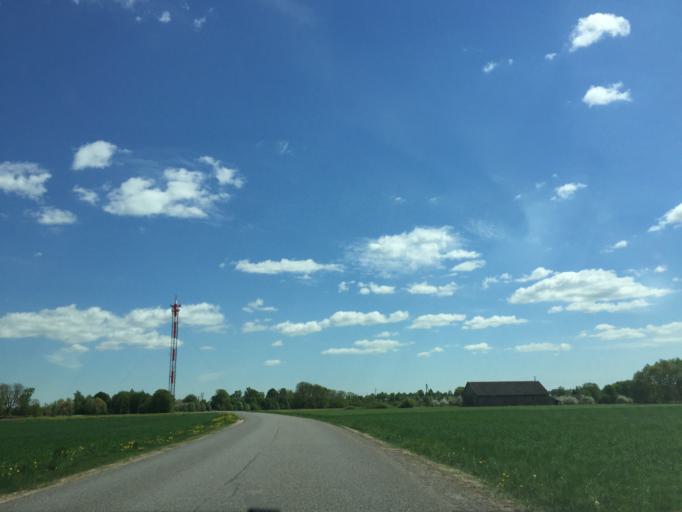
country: LV
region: Bauskas Rajons
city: Bauska
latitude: 56.4072
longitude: 24.1537
